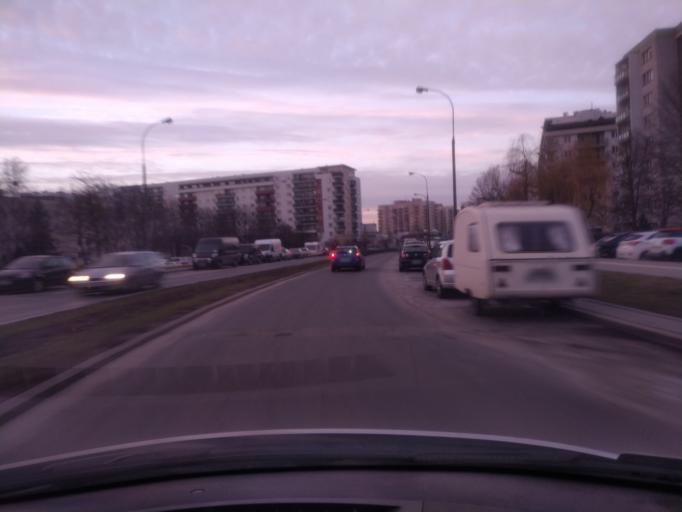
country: PL
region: Masovian Voivodeship
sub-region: Warszawa
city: Praga Poludnie
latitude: 52.2239
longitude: 21.0841
